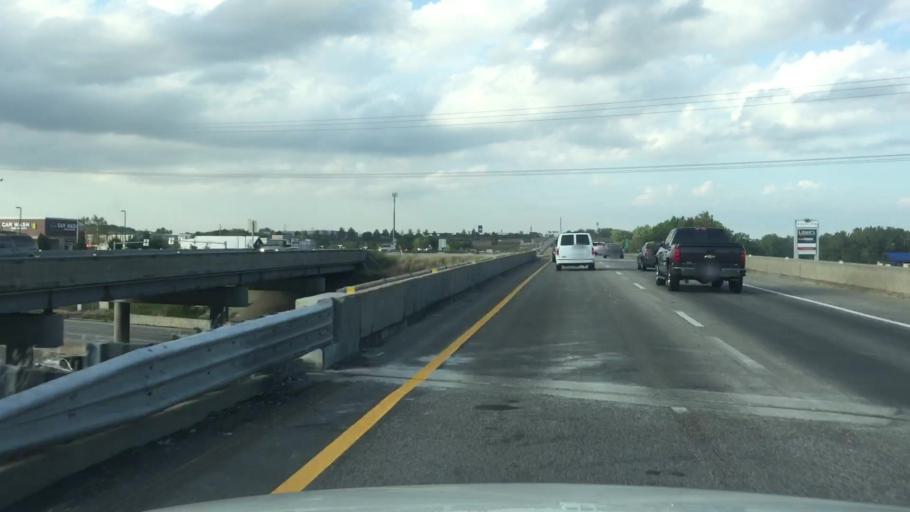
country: US
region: Missouri
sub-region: Jackson County
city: East Independence
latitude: 39.0330
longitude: -94.3612
